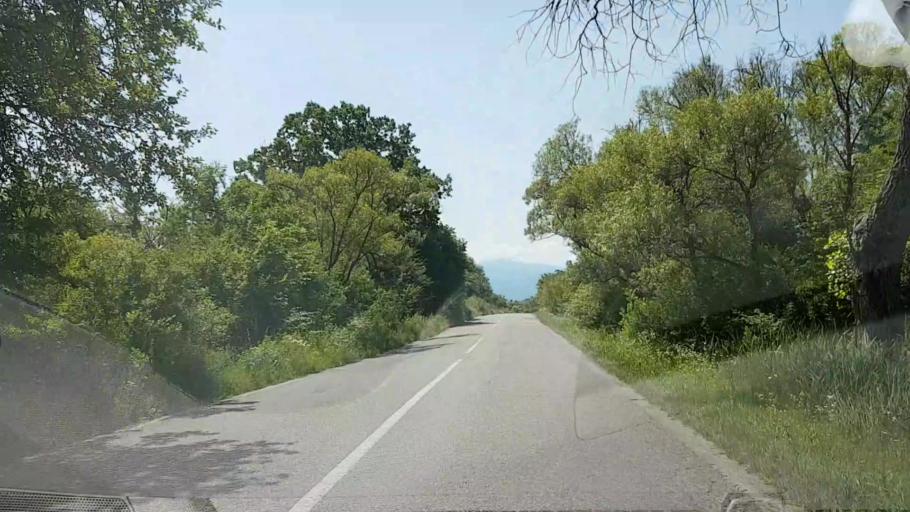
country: RO
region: Brasov
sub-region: Comuna Voila
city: Voila
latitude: 45.8660
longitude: 24.8249
